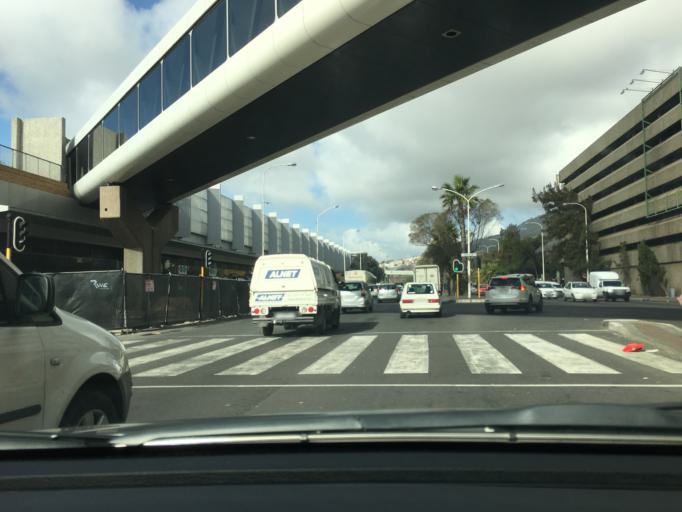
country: ZA
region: Western Cape
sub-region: City of Cape Town
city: Cape Town
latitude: -33.9228
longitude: 18.4242
